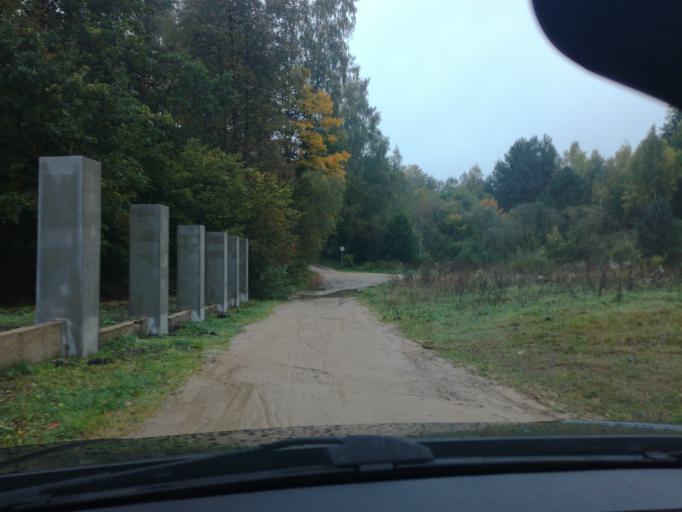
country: LT
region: Alytaus apskritis
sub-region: Alytus
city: Alytus
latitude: 54.3948
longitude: 24.0907
